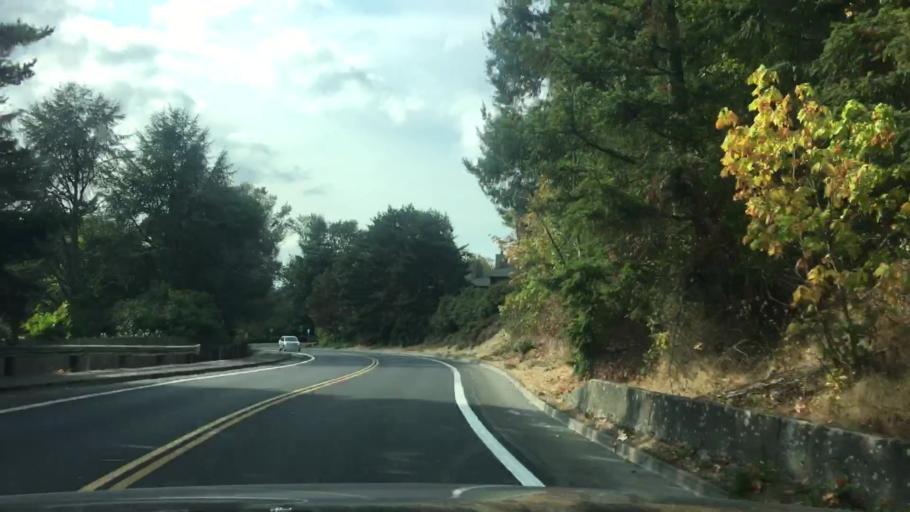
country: US
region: Oregon
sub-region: Lane County
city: Eugene
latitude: 44.0838
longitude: -123.0968
